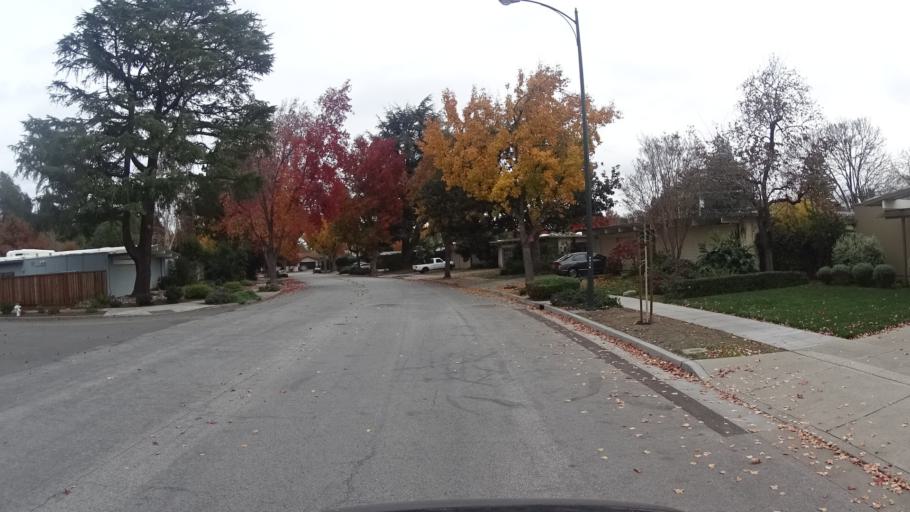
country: US
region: California
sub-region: Santa Clara County
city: Sunnyvale
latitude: 37.3551
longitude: -122.0477
